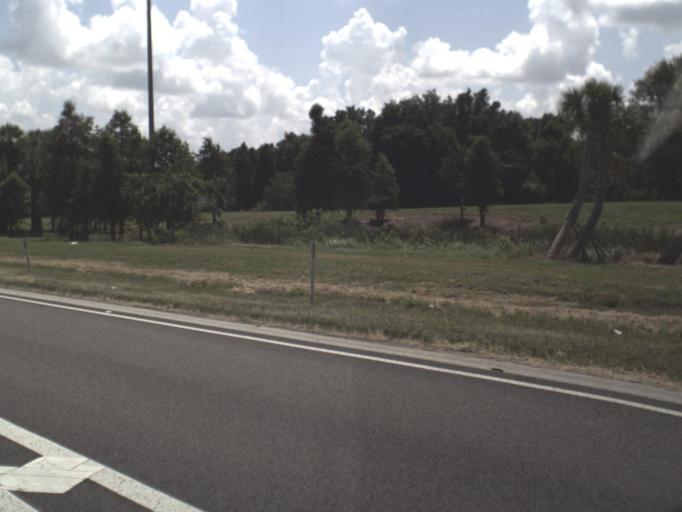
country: US
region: Florida
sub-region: Hillsborough County
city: Mango
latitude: 28.0023
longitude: -82.3243
